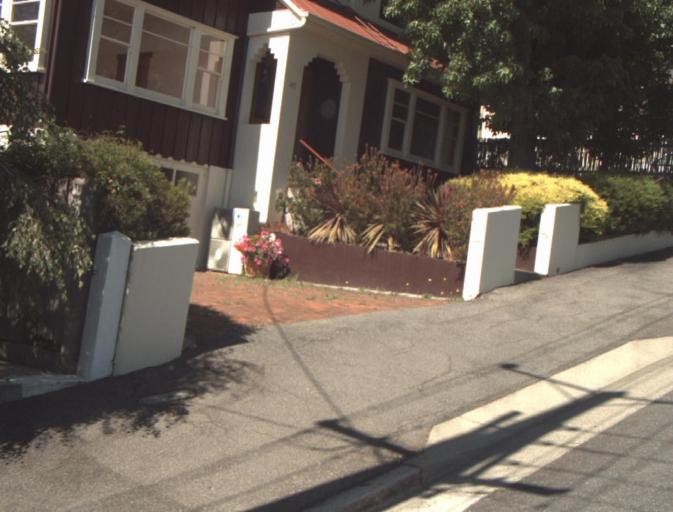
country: AU
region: Tasmania
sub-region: Launceston
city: West Launceston
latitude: -41.4459
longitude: 147.1324
